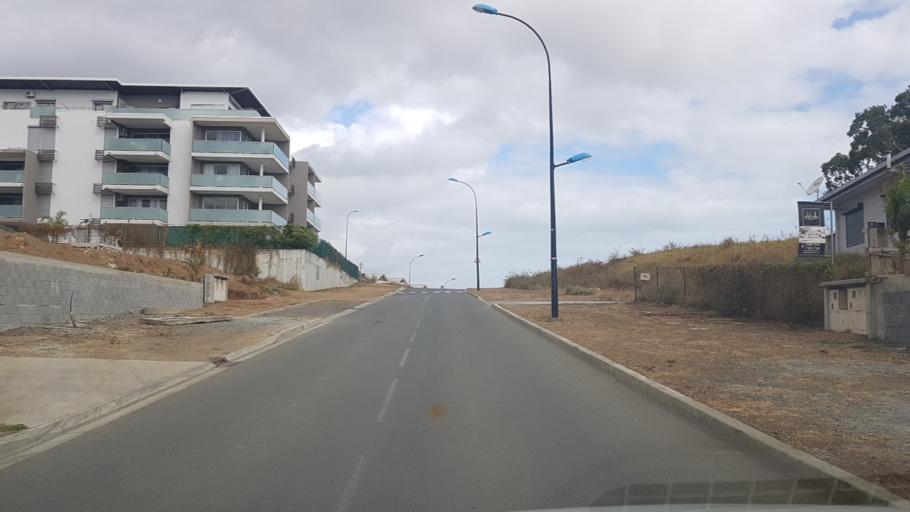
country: NC
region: South Province
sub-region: Dumbea
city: Dumbea
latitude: -22.2029
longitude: 166.4430
